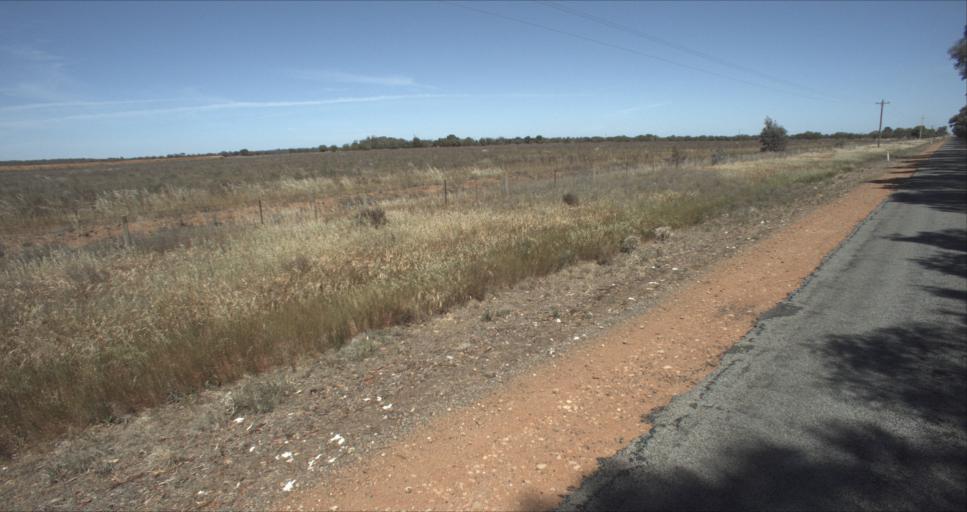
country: AU
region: New South Wales
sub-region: Leeton
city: Leeton
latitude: -34.5794
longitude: 146.2768
